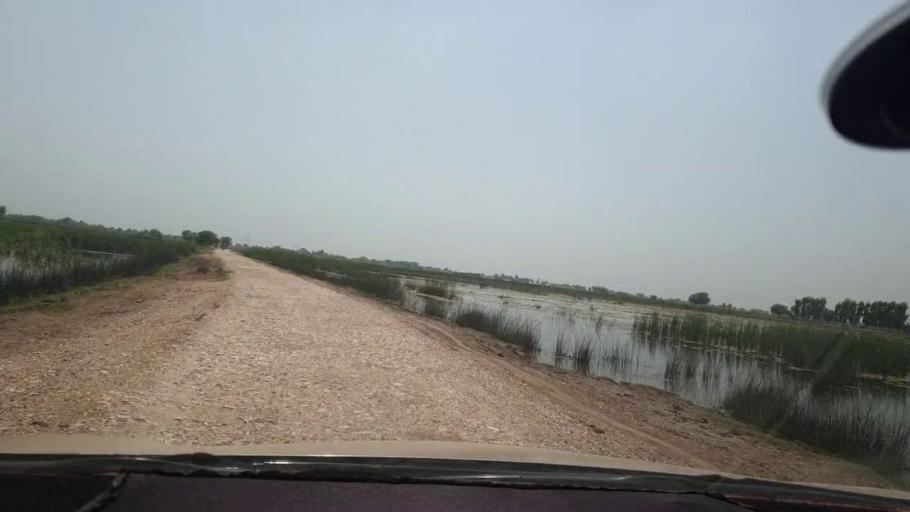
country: PK
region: Sindh
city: Kambar
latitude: 27.6488
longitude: 67.9321
